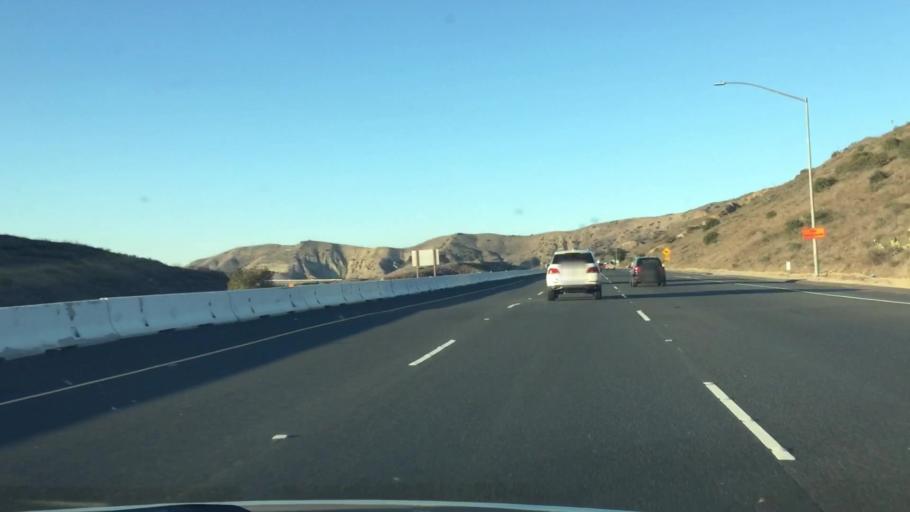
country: US
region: California
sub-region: Orange County
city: Foothill Ranch
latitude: 33.7257
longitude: -117.7190
